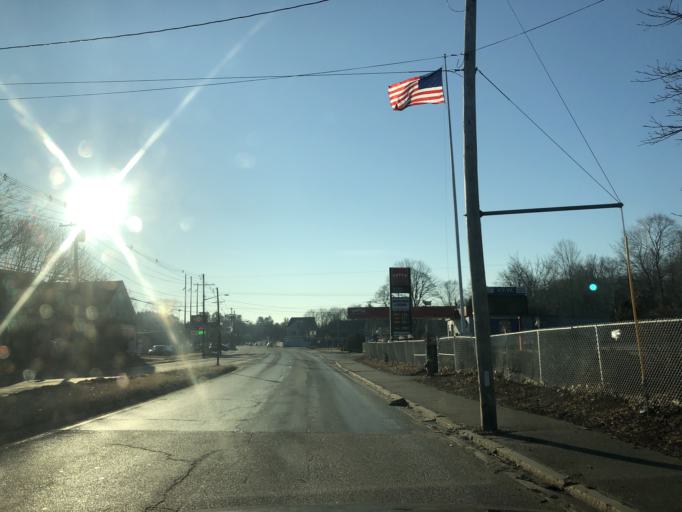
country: US
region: Massachusetts
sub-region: Norfolk County
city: Avon
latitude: 42.1238
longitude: -71.0349
